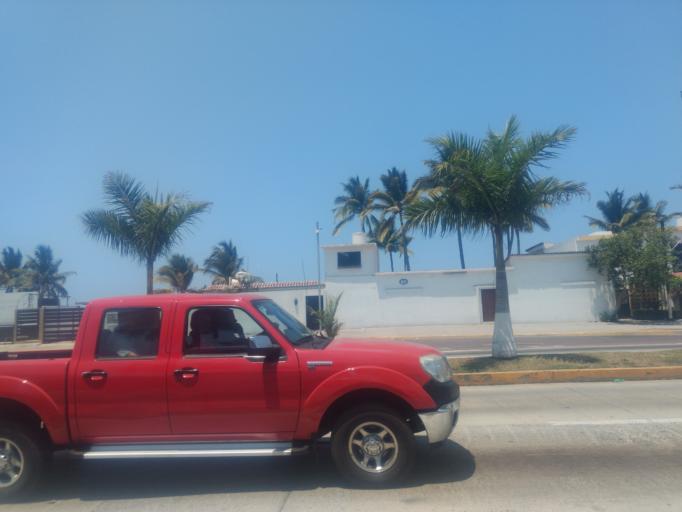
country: MX
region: Colima
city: Tapeixtles
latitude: 19.0909
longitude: -104.3143
